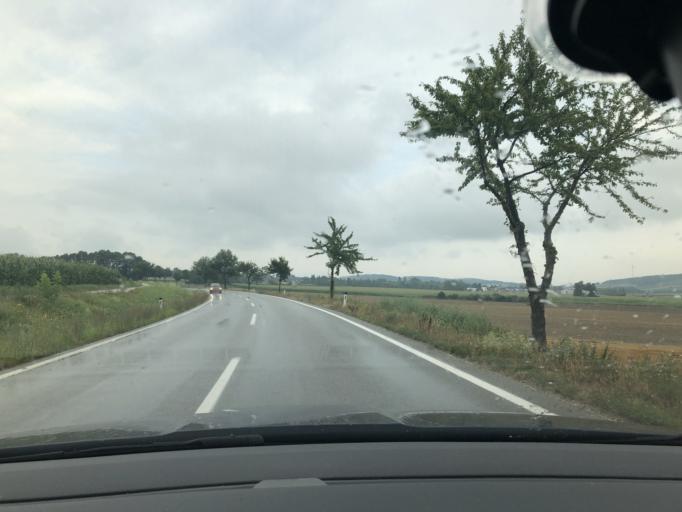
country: AT
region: Lower Austria
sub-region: Politischer Bezirk Ganserndorf
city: Gross-Schweinbarth
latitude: 48.4030
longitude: 16.6443
